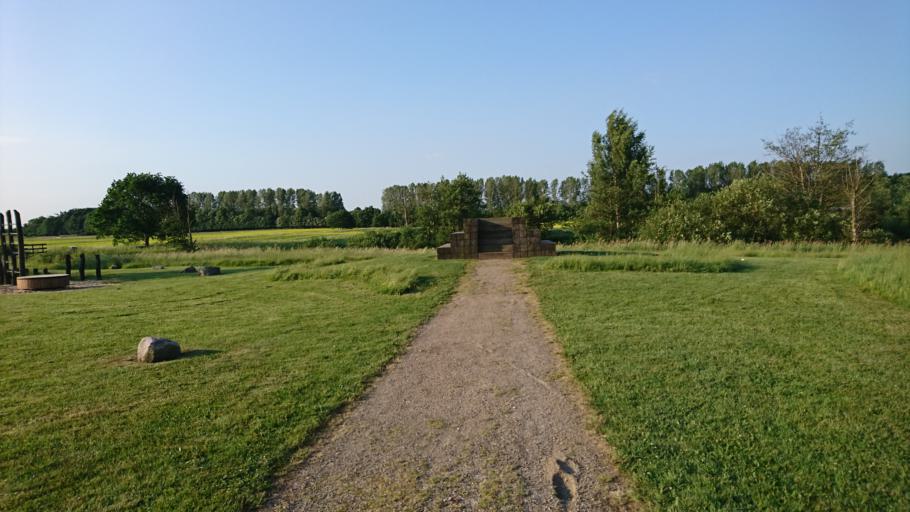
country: DK
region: Capital Region
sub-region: Ballerup Kommune
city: Ballerup
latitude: 55.7111
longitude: 12.3598
